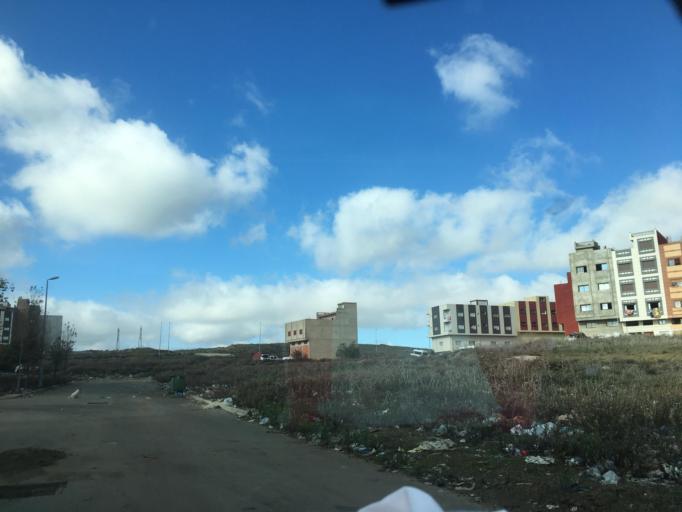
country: MA
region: Tanger-Tetouan
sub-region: Tanger-Assilah
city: Tangier
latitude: 35.7092
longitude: -5.8158
